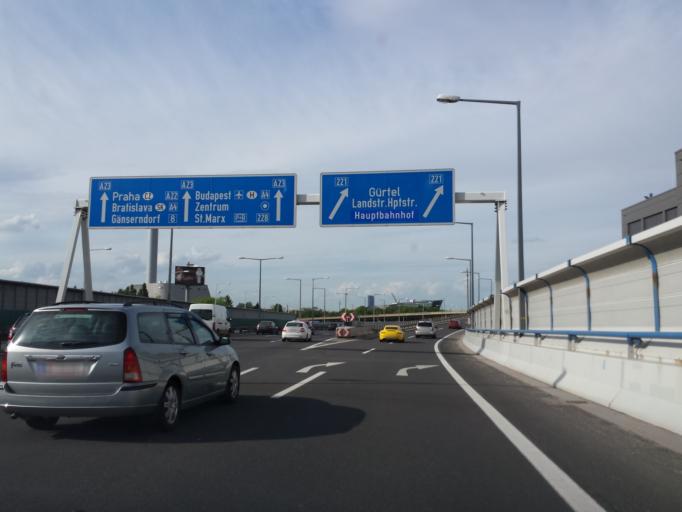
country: AT
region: Vienna
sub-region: Wien Stadt
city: Vienna
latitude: 48.1772
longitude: 16.4002
